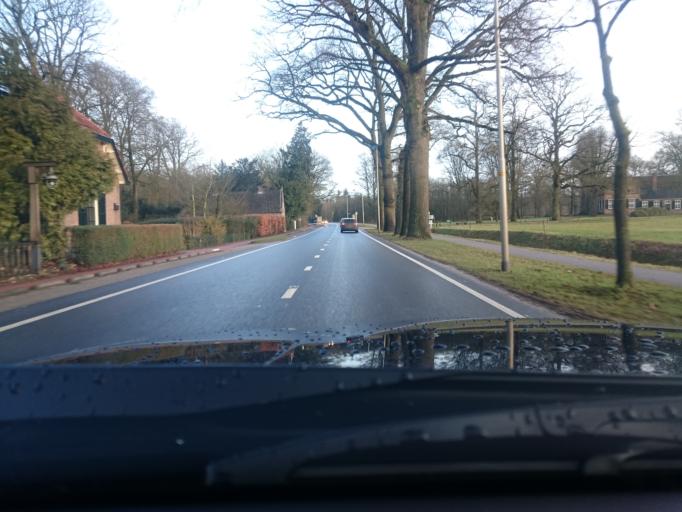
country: NL
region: Gelderland
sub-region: Gemeente Voorst
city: Voorst
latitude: 52.1763
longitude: 6.1403
